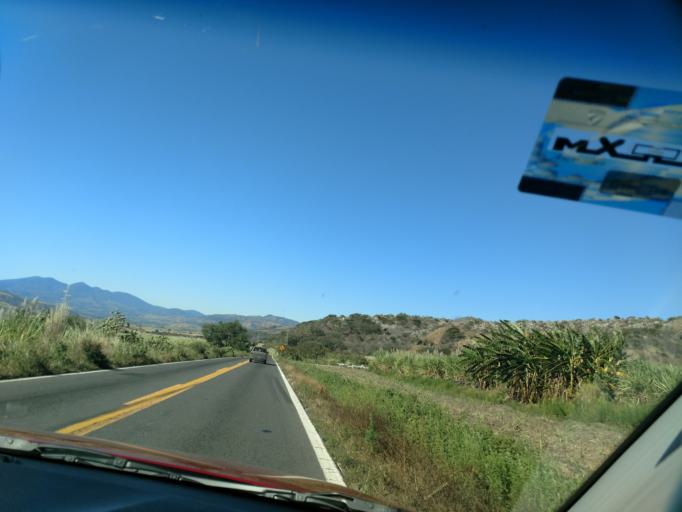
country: MX
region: Nayarit
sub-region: Ahuacatlan
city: Ahuacatlan
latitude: 21.1073
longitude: -104.5868
